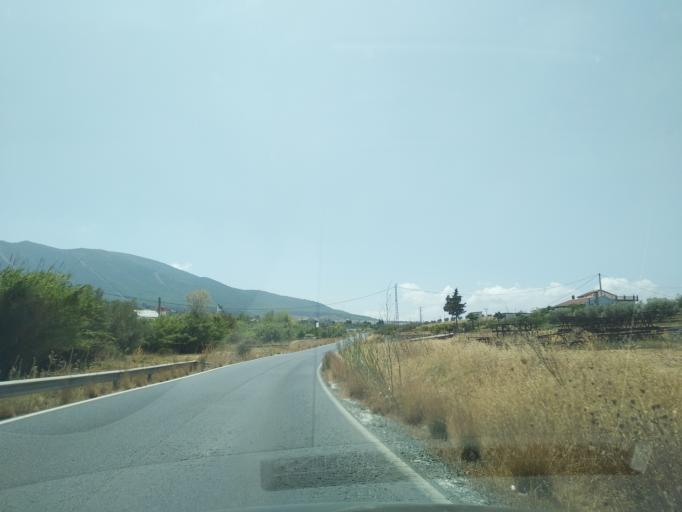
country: ES
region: Andalusia
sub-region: Provincia de Malaga
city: Alhaurin el Grande
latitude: 36.6660
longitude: -4.6685
